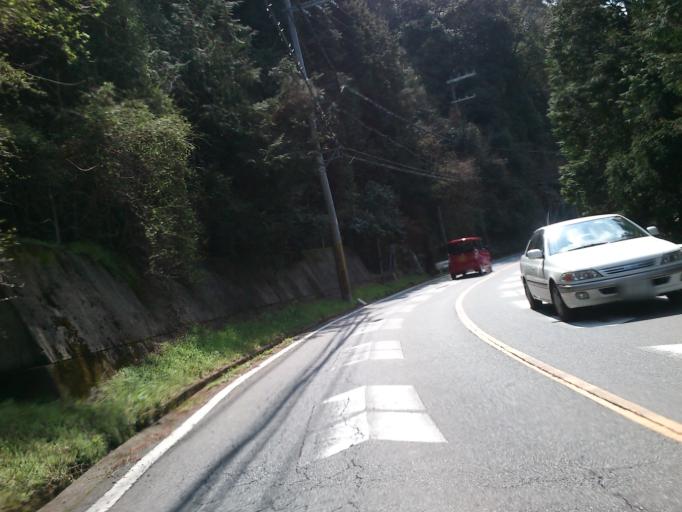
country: JP
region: Kyoto
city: Tanabe
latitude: 34.7831
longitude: 135.8870
